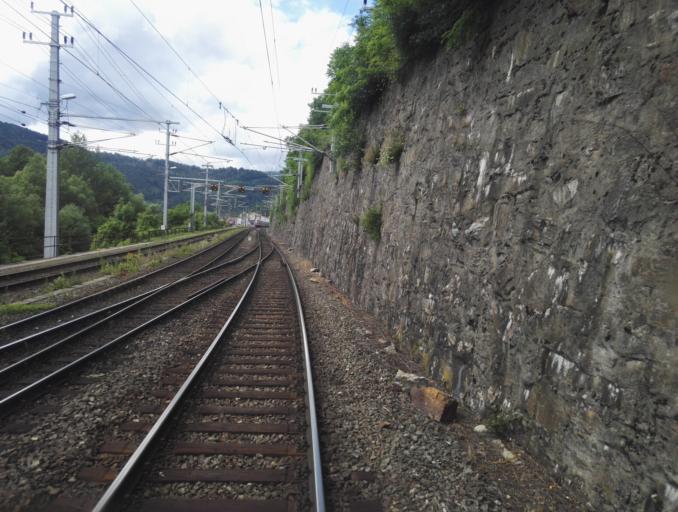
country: AT
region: Styria
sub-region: Politischer Bezirk Bruck-Muerzzuschlag
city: Bruck an der Mur
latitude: 47.4190
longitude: 15.2809
